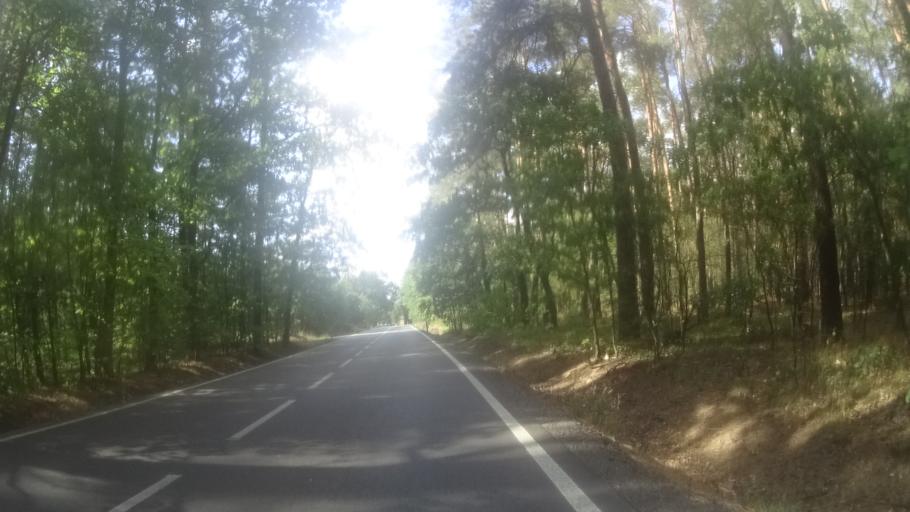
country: CZ
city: Borohradek
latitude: 50.1099
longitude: 16.0769
